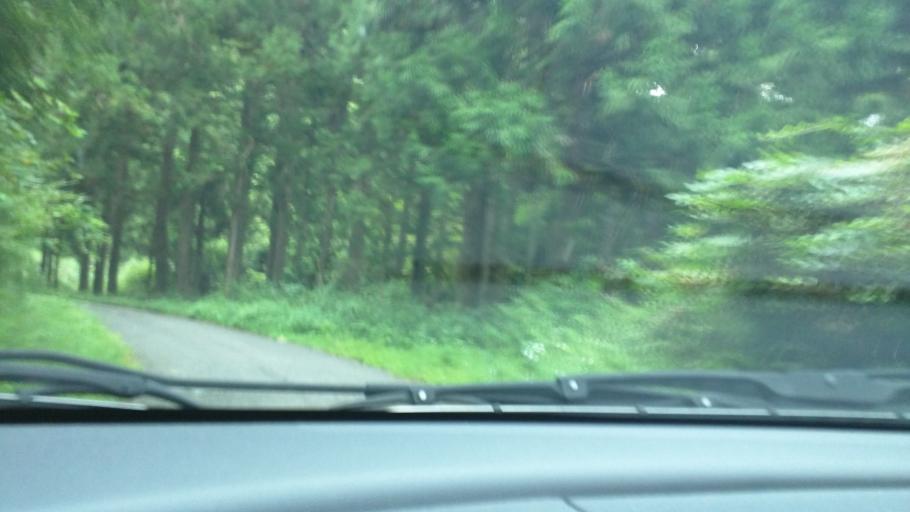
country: JP
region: Fukushima
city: Kitakata
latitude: 37.4352
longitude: 139.6760
